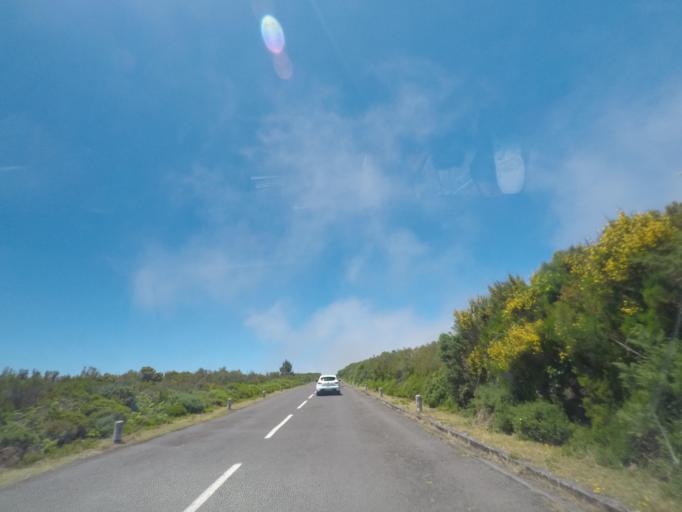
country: PT
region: Madeira
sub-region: Porto Moniz
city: Porto Moniz
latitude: 32.8050
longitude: -17.1914
